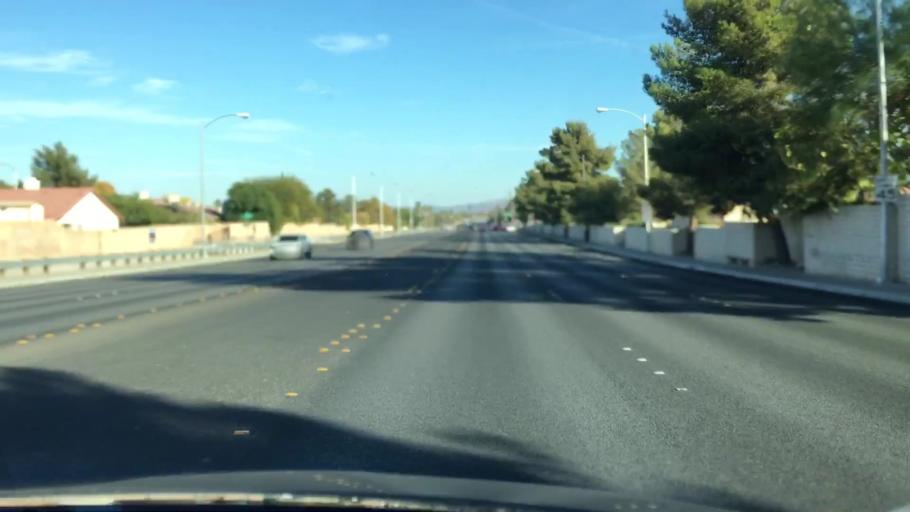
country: US
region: Nevada
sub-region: Clark County
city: Paradise
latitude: 36.0424
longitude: -115.1487
